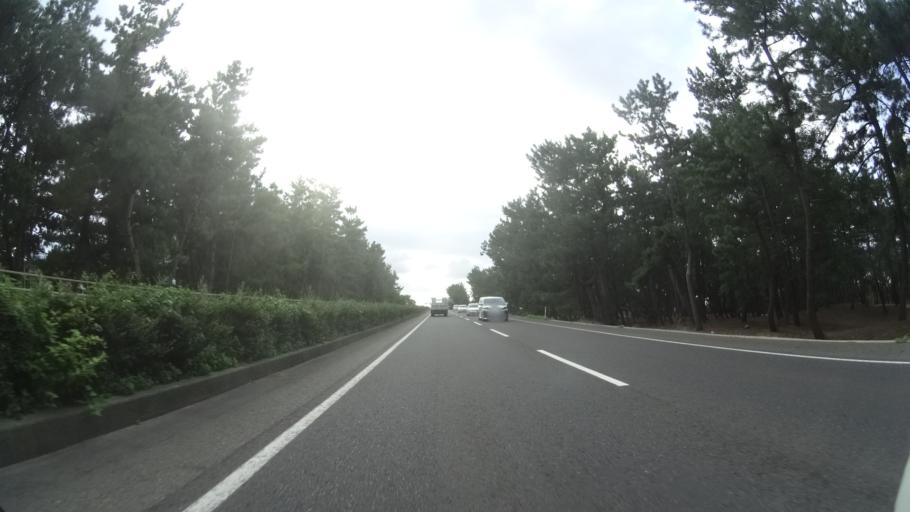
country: JP
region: Tottori
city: Kurayoshi
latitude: 35.4997
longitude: 133.7593
